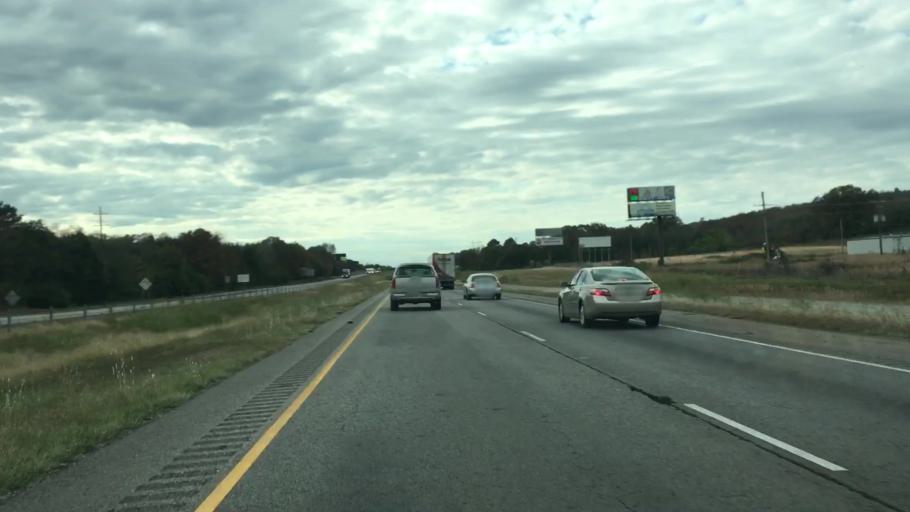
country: US
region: Arkansas
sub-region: Conway County
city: Morrilton
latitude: 35.1630
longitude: -92.6430
